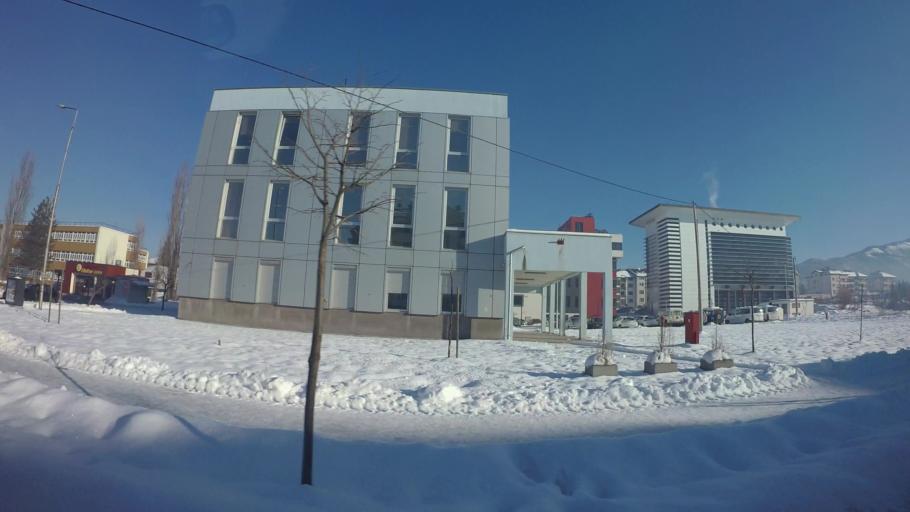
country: BA
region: Federation of Bosnia and Herzegovina
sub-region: Kanton Sarajevo
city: Sarajevo
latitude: 43.8220
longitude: 18.3647
